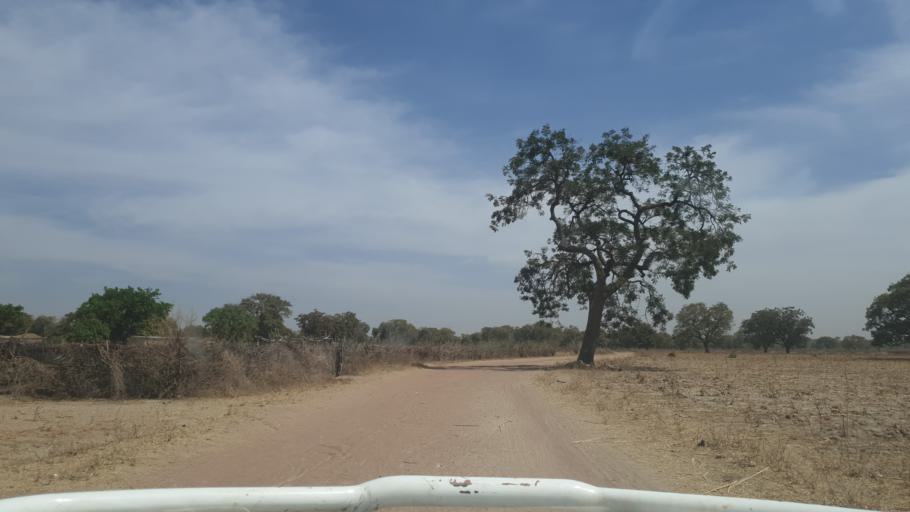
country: ML
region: Sikasso
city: Yorosso
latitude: 12.2948
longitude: -4.6430
